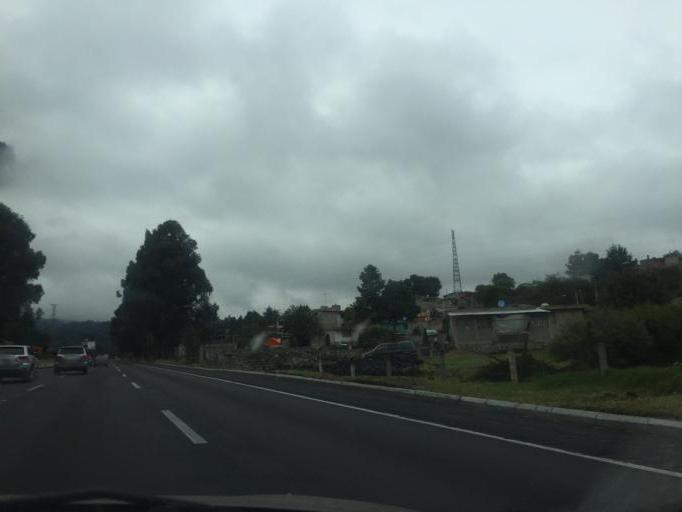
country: MX
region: Mexico City
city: Xochimilco
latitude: 19.1976
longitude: -99.1490
